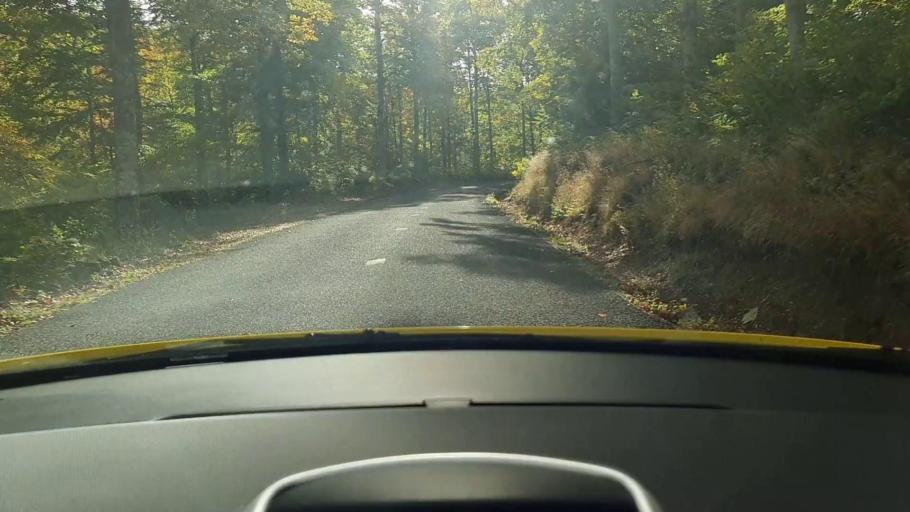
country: FR
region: Languedoc-Roussillon
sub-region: Departement du Gard
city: Valleraugue
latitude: 44.0713
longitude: 3.5685
